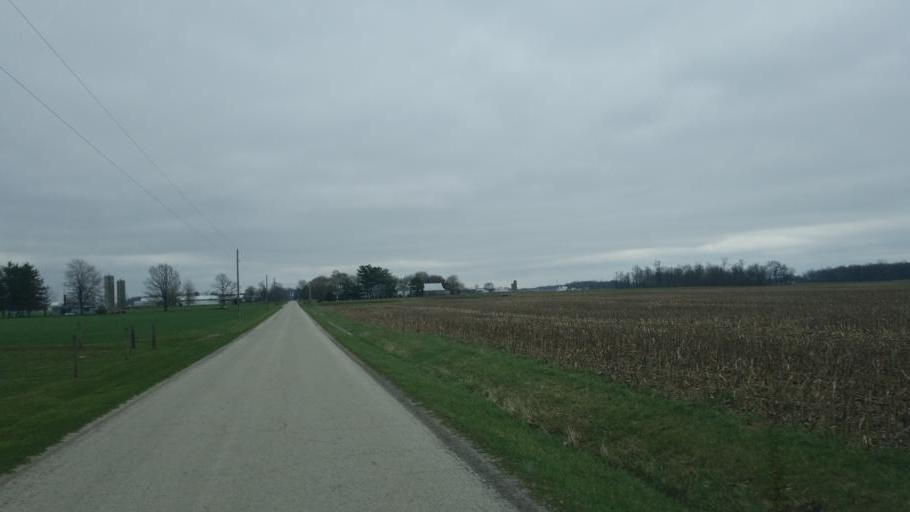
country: US
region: Ohio
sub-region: Crawford County
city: Bucyrus
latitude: 40.8488
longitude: -83.0076
